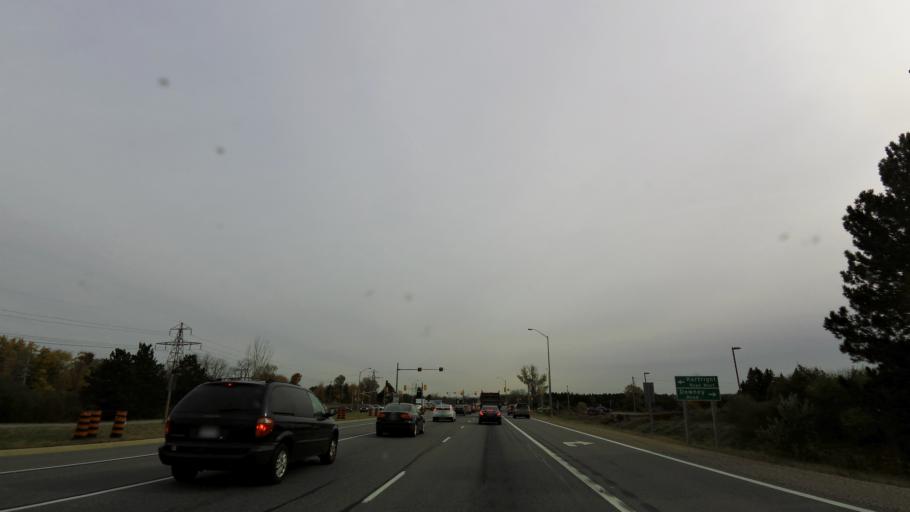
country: CA
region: Ontario
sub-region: Wellington County
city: Guelph
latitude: 43.5071
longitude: -80.2360
